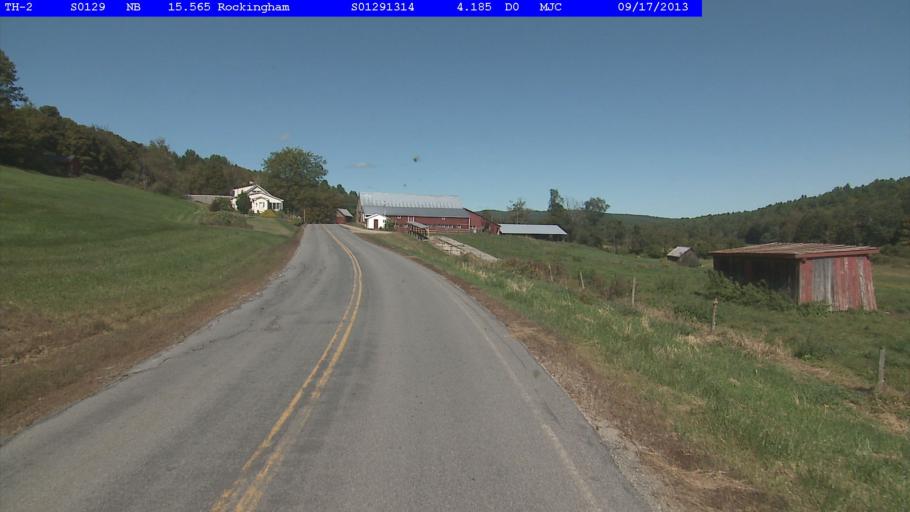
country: US
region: Vermont
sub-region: Windham County
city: Rockingham
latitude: 43.1773
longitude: -72.5158
